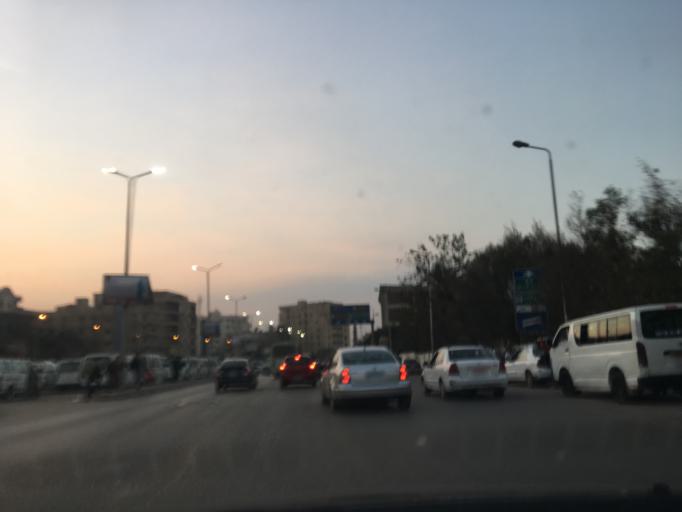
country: EG
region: Al Jizah
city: Al Jizah
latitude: 29.9906
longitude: 31.1328
